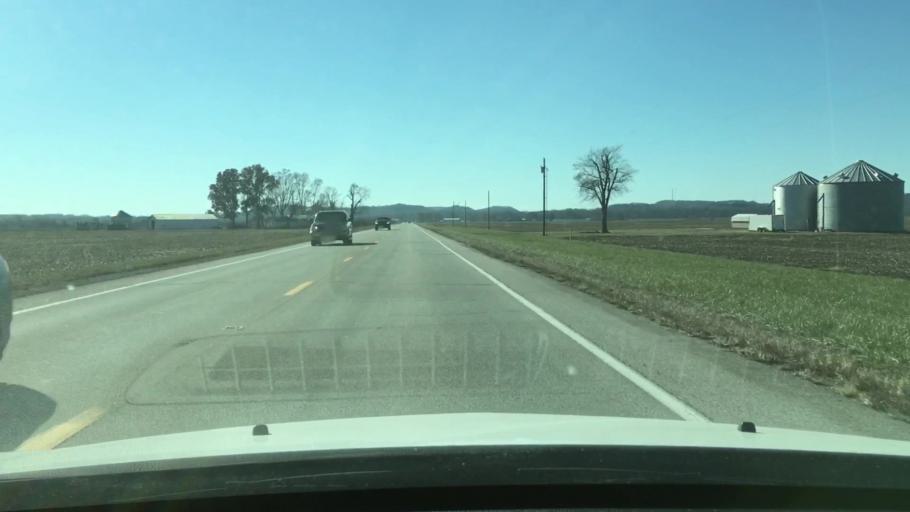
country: US
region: Missouri
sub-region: Pike County
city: Louisiana
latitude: 39.4795
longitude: -91.0181
